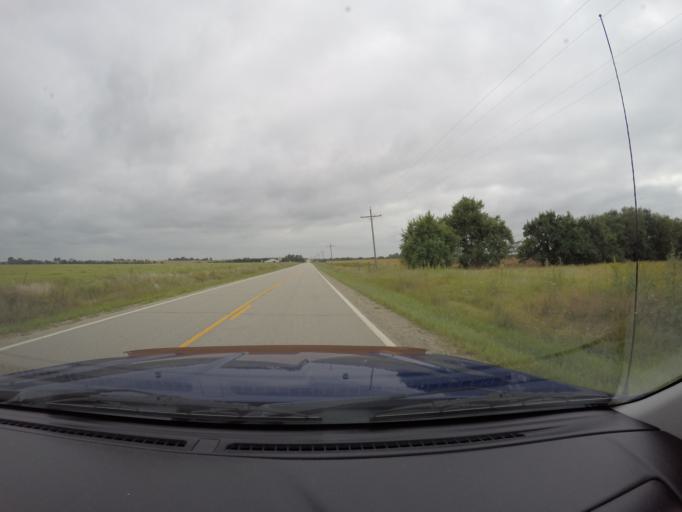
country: US
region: Kansas
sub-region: Morris County
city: Council Grove
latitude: 38.8362
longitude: -96.5941
